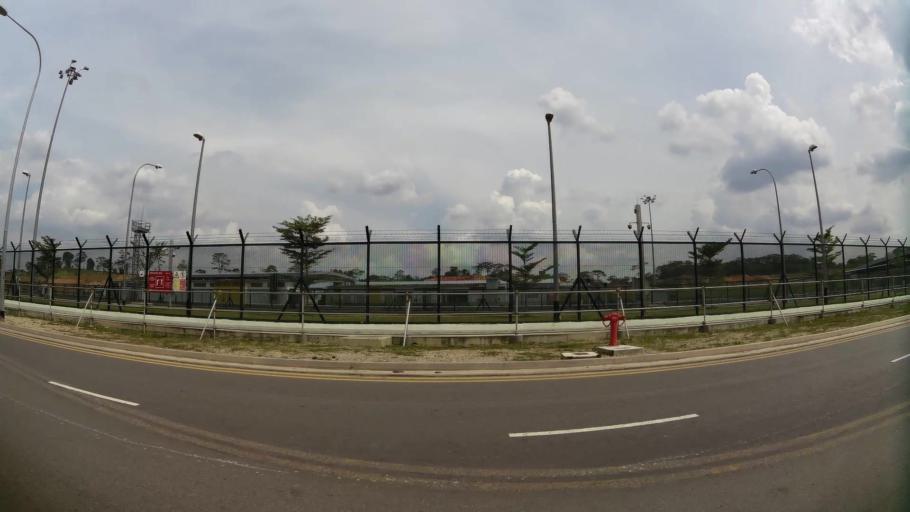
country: MY
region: Johor
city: Johor Bahru
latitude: 1.3996
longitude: 103.7556
